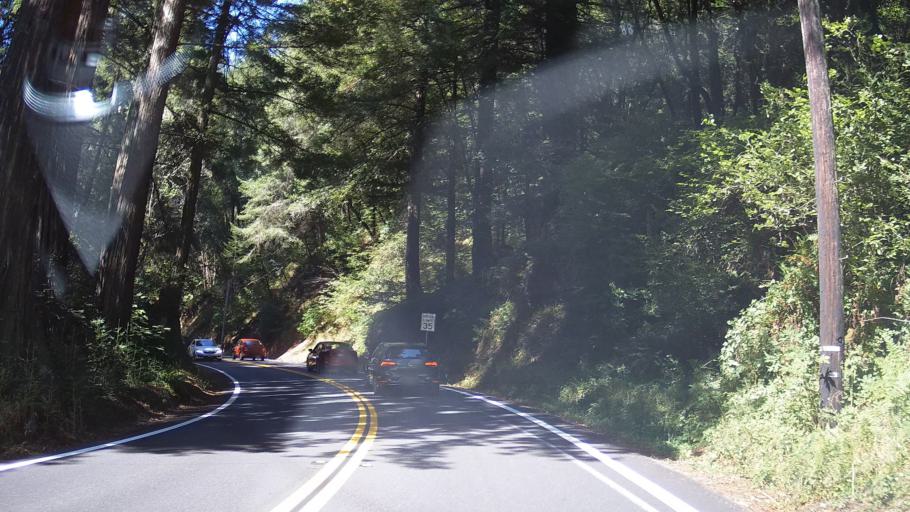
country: US
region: California
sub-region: Marin County
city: Lagunitas-Forest Knolls
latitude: 38.0180
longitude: -122.7241
